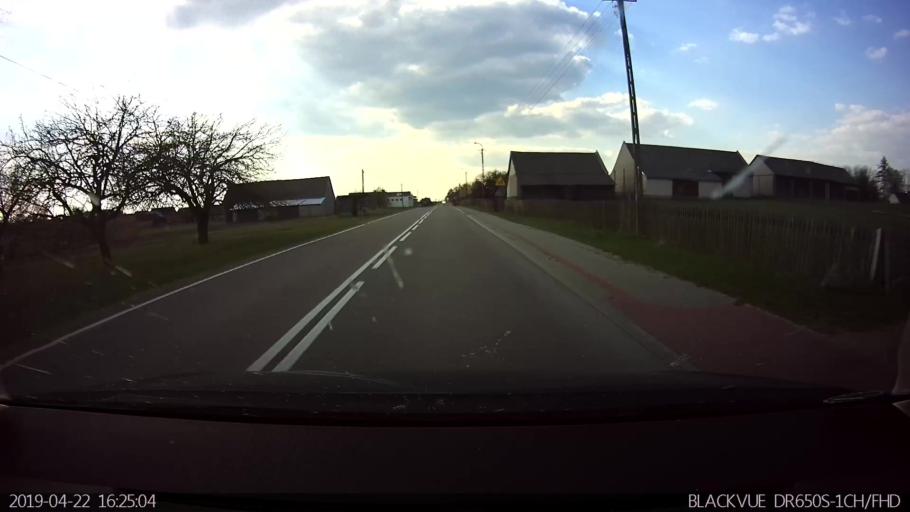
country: PL
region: Podlasie
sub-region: Powiat hajnowski
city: Kleszczele
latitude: 52.5542
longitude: 23.2506
